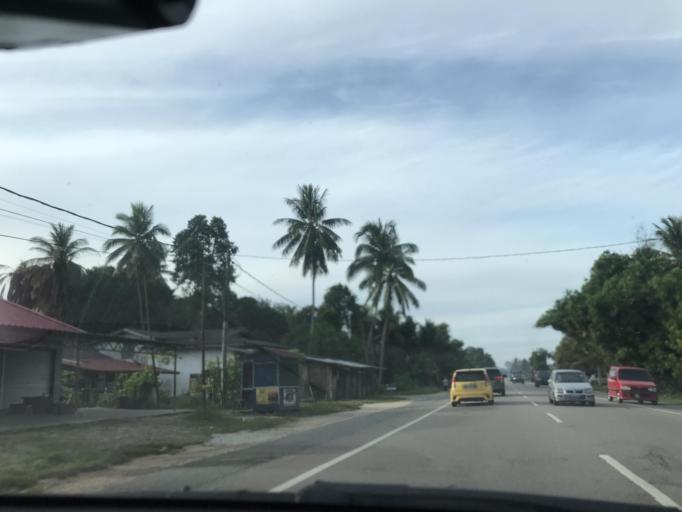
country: MY
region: Kelantan
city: Ketereh
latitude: 5.9785
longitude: 102.1910
